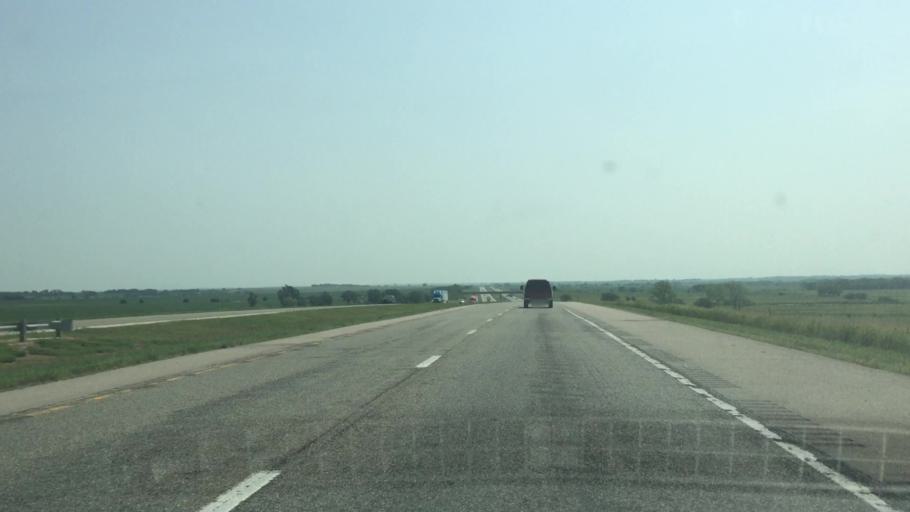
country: US
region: Kansas
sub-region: Osage County
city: Osage City
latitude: 38.4258
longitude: -95.8321
